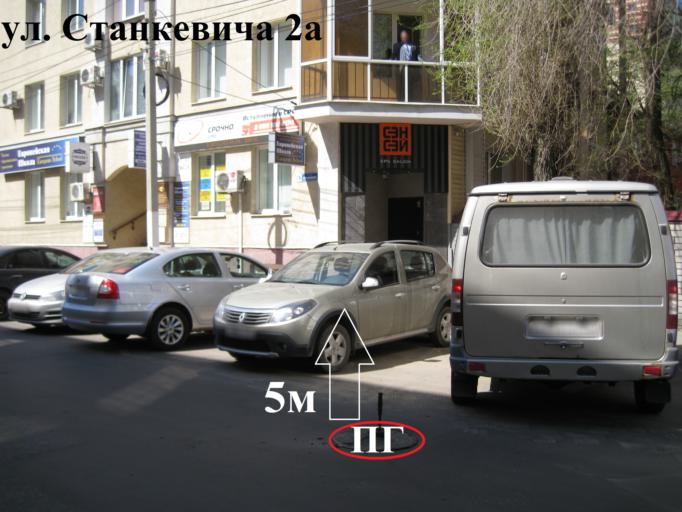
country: RU
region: Voronezj
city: Voronezh
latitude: 51.6587
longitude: 39.1984
